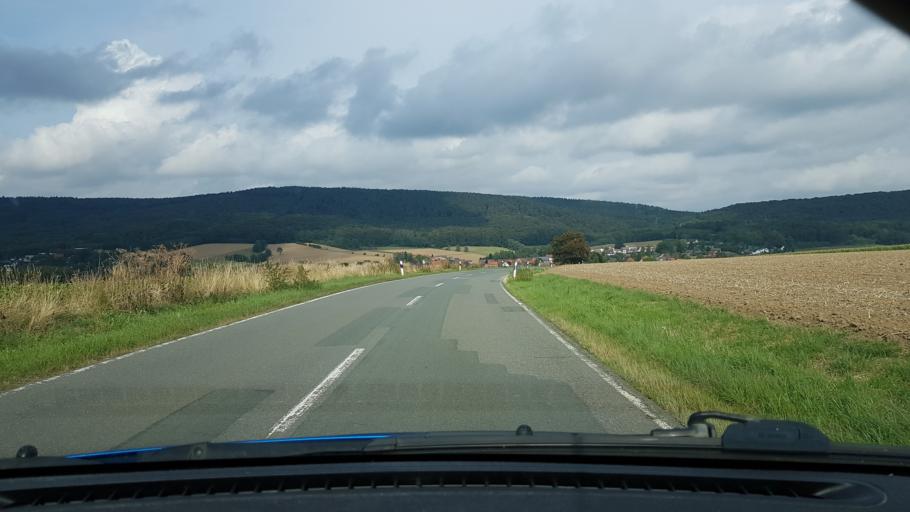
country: DE
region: Lower Saxony
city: Barsinghausen
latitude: 52.2495
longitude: 9.4422
